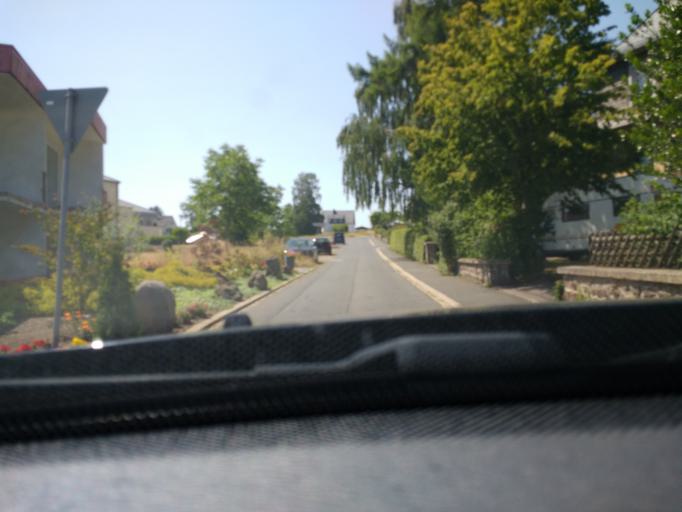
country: DE
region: Rheinland-Pfalz
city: Manderscheid
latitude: 50.0936
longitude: 6.8063
